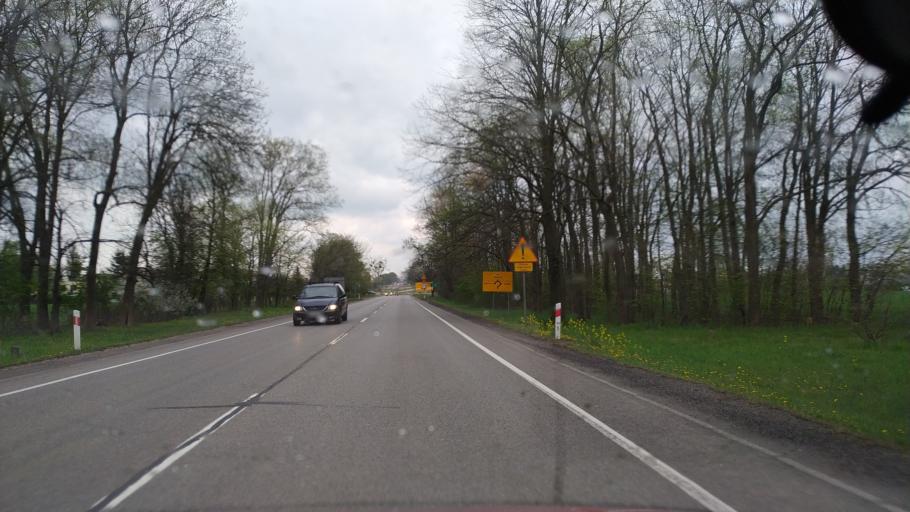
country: PL
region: Pomeranian Voivodeship
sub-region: Powiat tczewski
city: Subkowy
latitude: 54.0485
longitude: 18.7536
